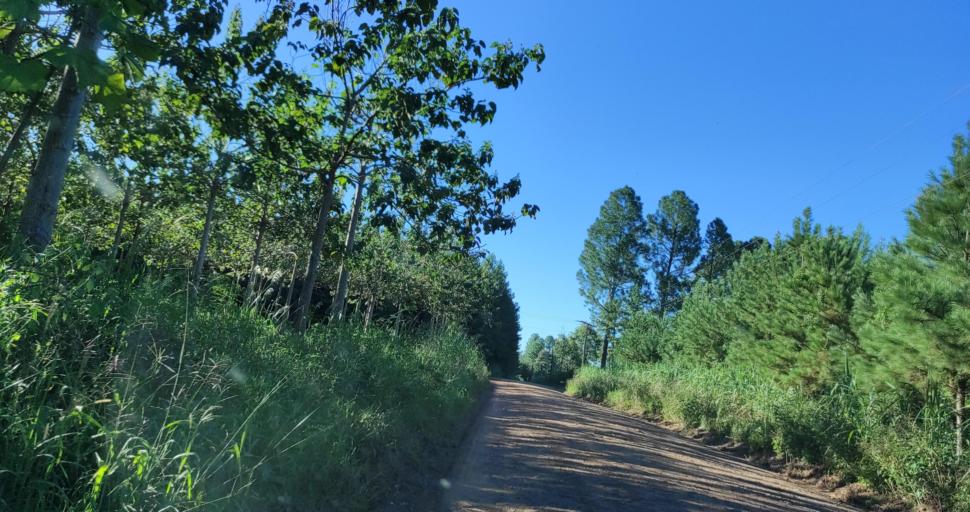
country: AR
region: Misiones
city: Garuhape
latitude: -26.8808
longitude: -54.9963
